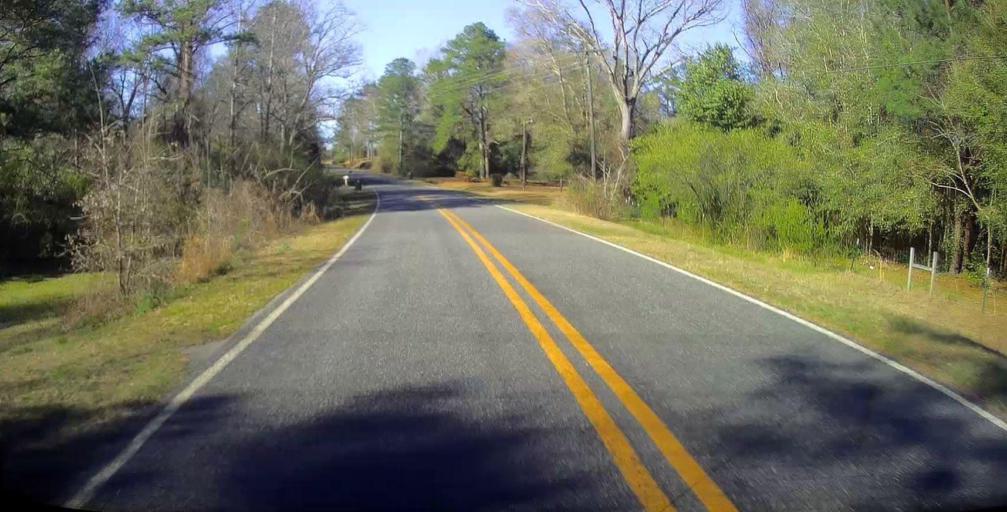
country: US
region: Georgia
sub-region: Peach County
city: Fort Valley
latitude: 32.5880
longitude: -83.8513
